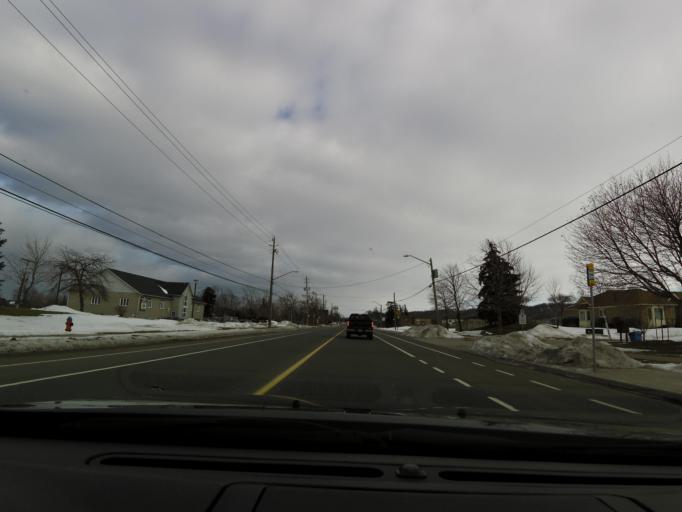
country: CA
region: Ontario
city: Hamilton
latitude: 43.2141
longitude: -79.7069
